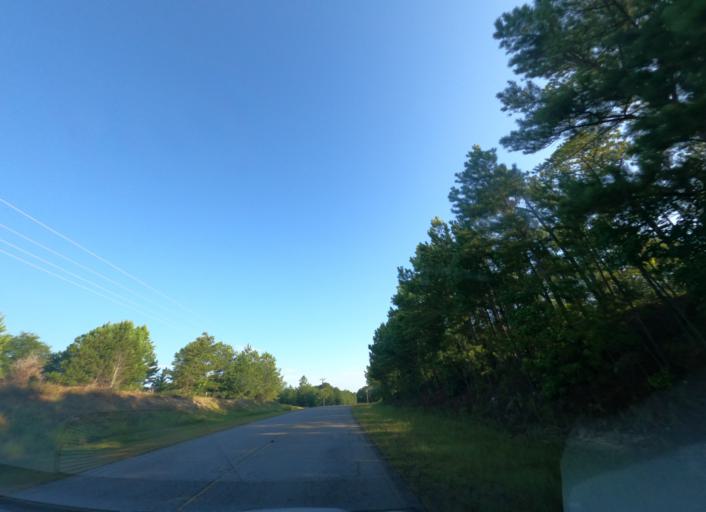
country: US
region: Georgia
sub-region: Lincoln County
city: Lincolnton
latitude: 33.8045
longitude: -82.4070
